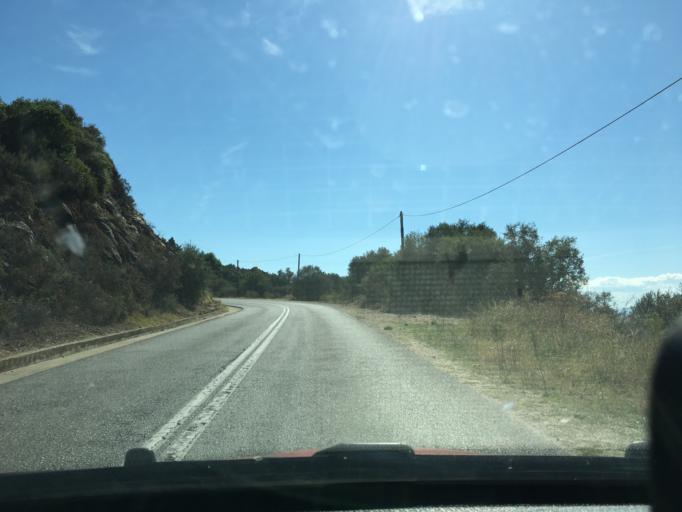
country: GR
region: Central Macedonia
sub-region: Nomos Chalkidikis
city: Ouranoupolis
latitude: 40.3376
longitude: 23.9712
